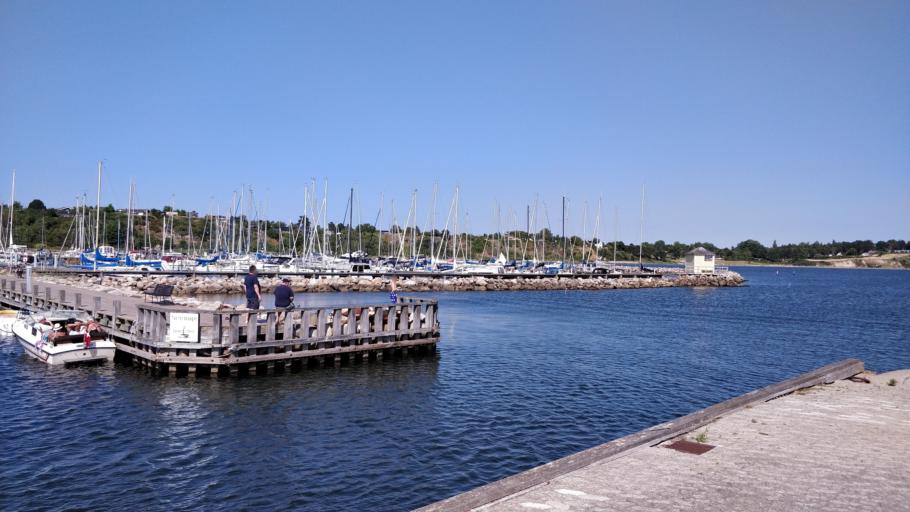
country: DK
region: Capital Region
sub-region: Halsnaes Kommune
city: Hundested
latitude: 55.9411
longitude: 11.8667
